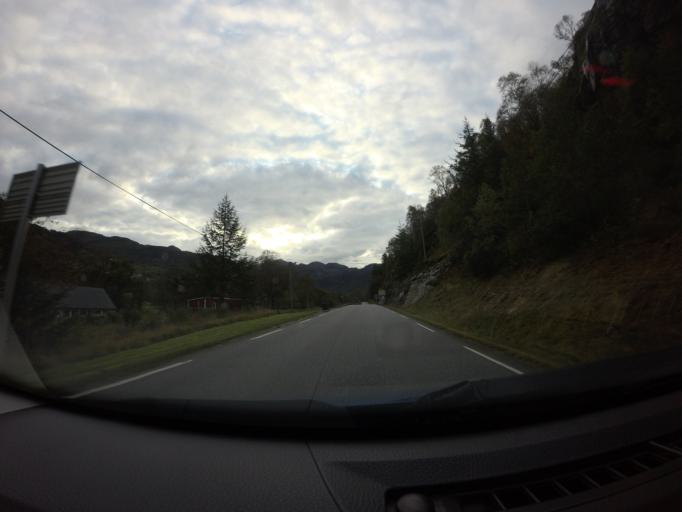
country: NO
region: Rogaland
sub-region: Forsand
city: Forsand
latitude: 58.8058
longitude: 6.2513
